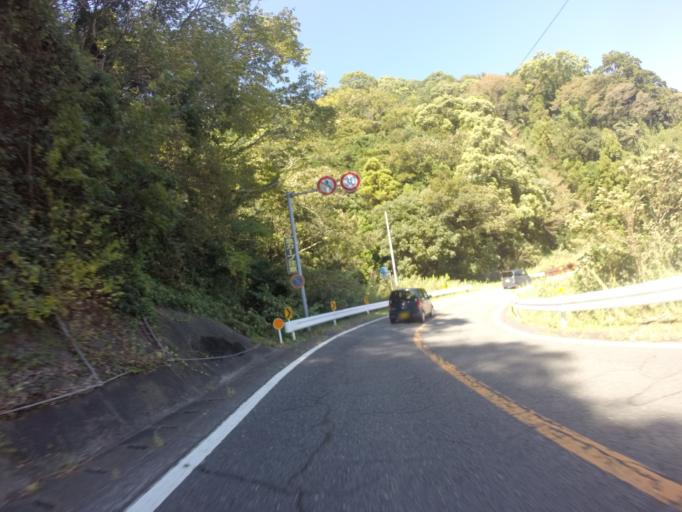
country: JP
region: Shizuoka
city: Yaizu
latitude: 34.9012
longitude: 138.3467
